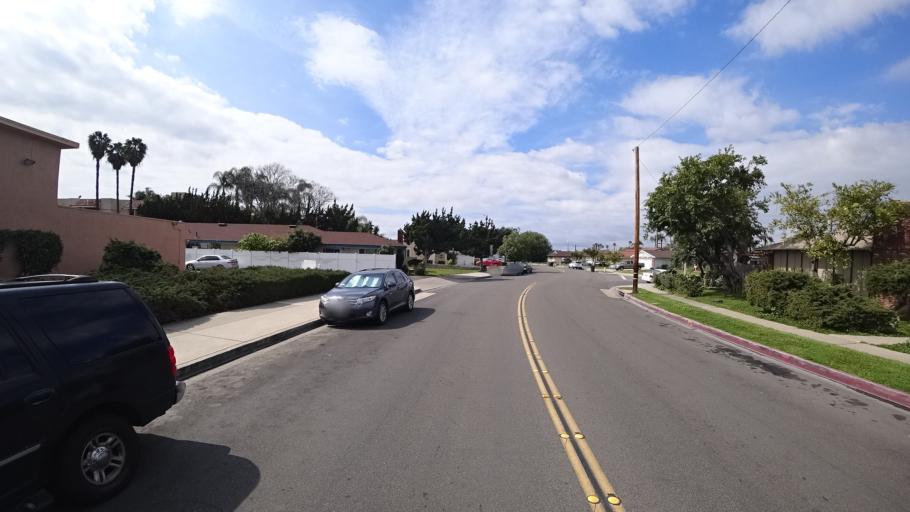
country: US
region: California
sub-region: Orange County
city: Stanton
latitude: 33.8342
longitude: -117.9831
